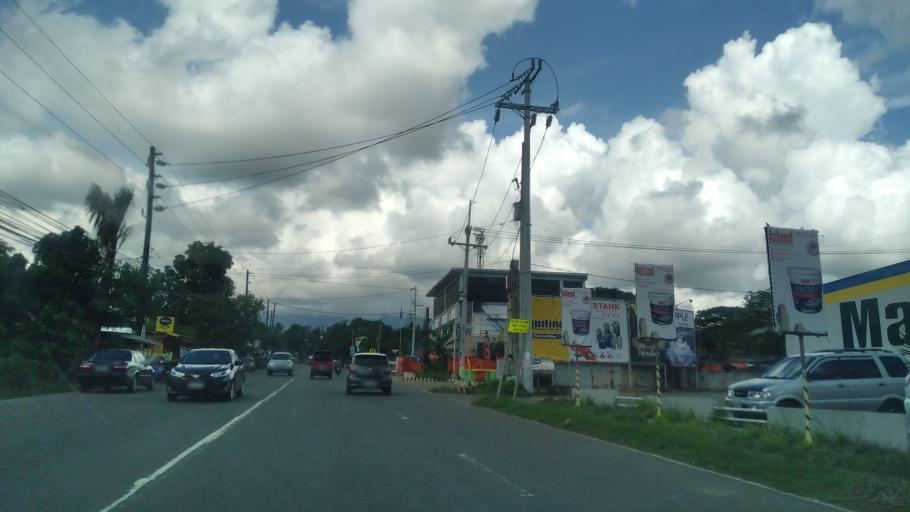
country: PH
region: Calabarzon
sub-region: Province of Quezon
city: Isabang
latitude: 13.9573
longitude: 121.5705
